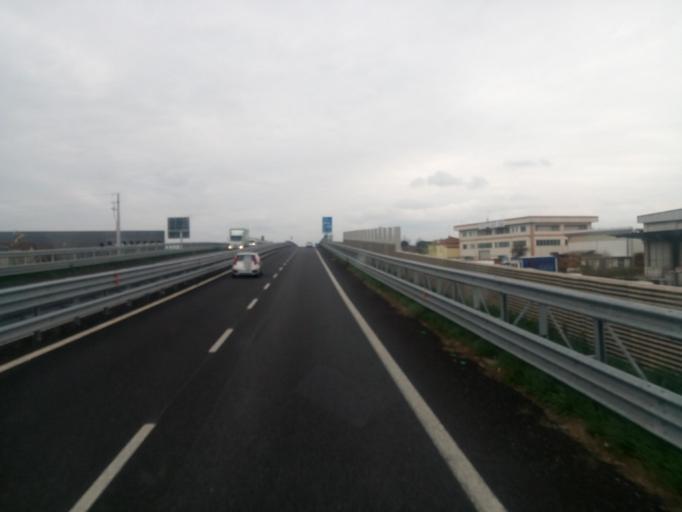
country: IT
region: Emilia-Romagna
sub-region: Forli-Cesena
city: Forli
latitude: 44.2232
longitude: 12.0838
